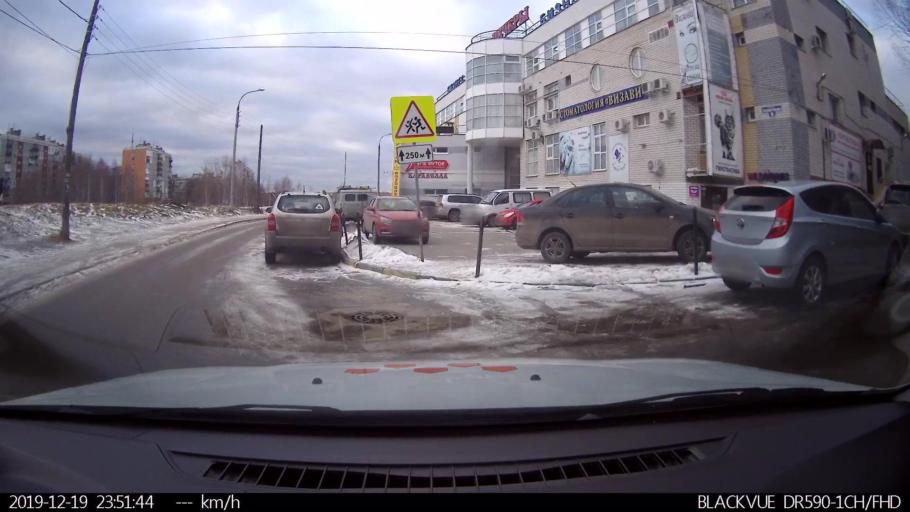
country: RU
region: Vologda
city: Kharovsk
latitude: 60.0237
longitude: 40.0433
